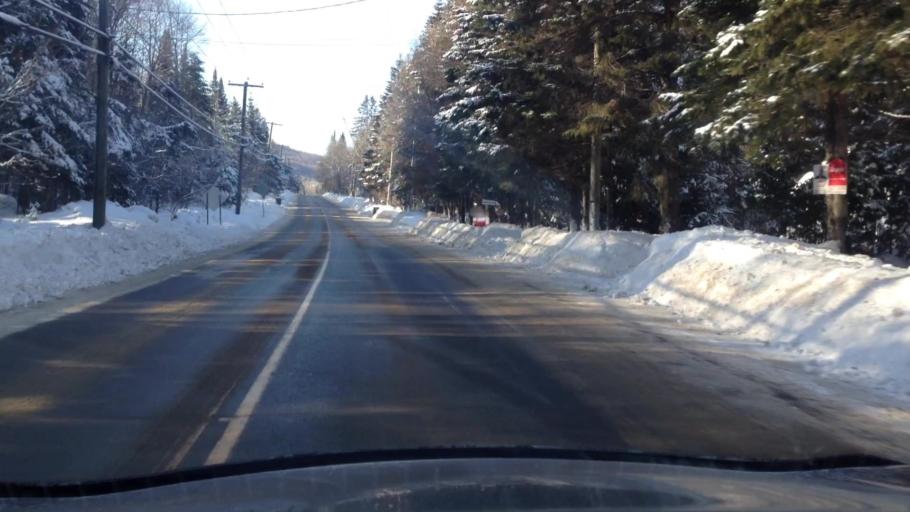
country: CA
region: Quebec
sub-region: Laurentides
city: Sainte-Agathe-des-Monts
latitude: 45.9294
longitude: -74.4083
